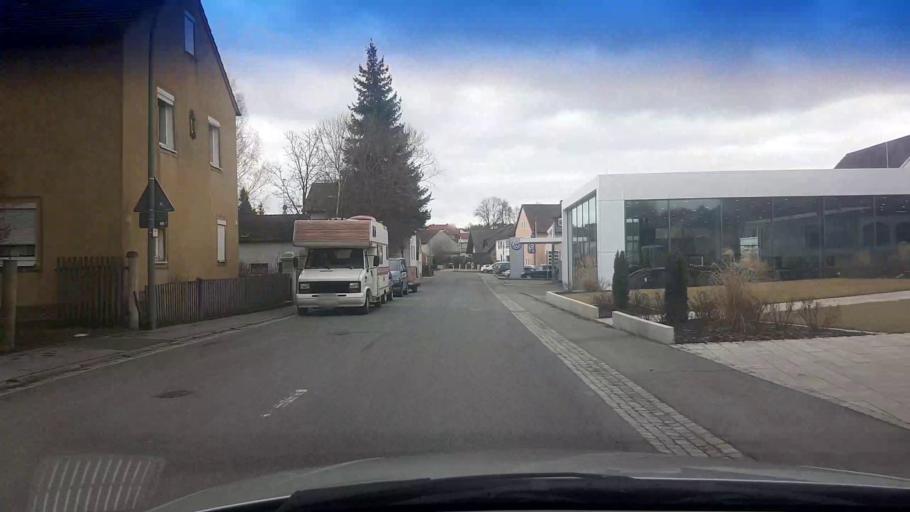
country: DE
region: Bavaria
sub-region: Upper Franconia
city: Priesendorf
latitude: 49.9190
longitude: 10.6788
